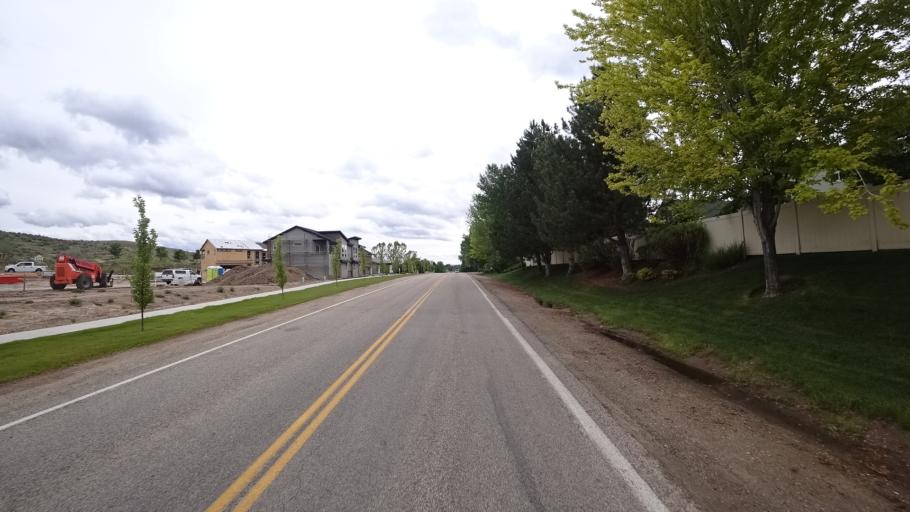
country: US
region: Idaho
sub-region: Ada County
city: Eagle
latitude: 43.7150
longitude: -116.3172
